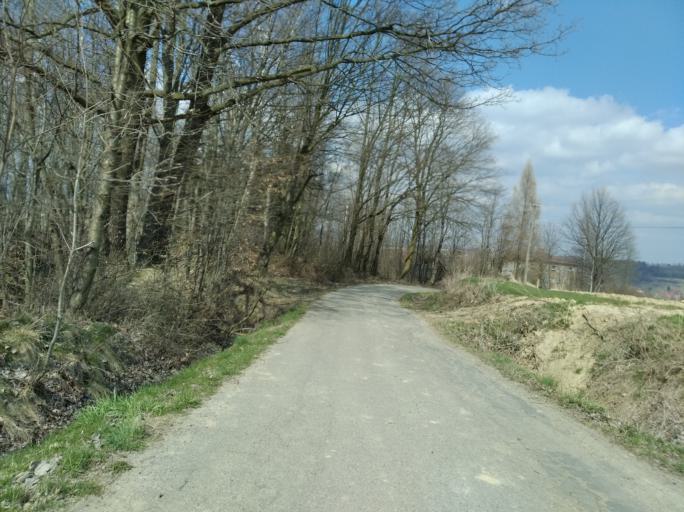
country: PL
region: Subcarpathian Voivodeship
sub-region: Powiat strzyzowski
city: Strzyzow
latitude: 49.8370
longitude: 21.8079
